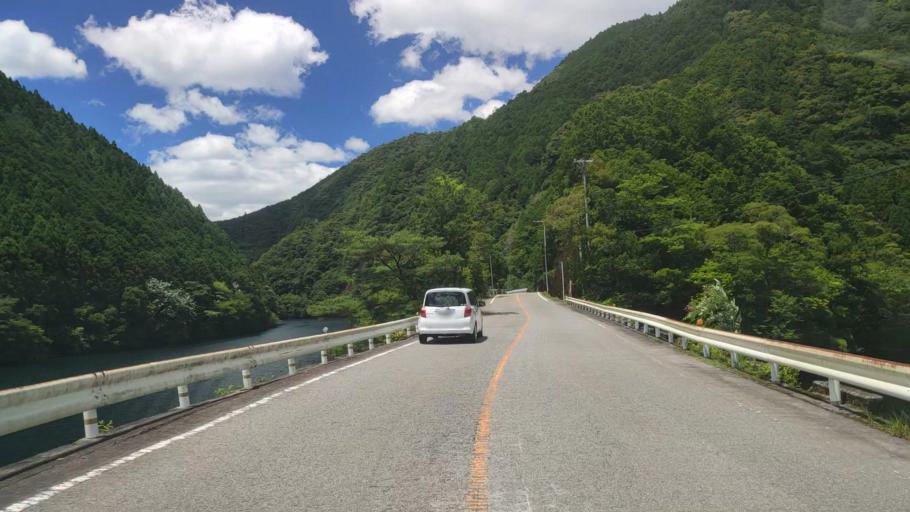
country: JP
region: Mie
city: Owase
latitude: 33.9963
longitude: 136.0244
